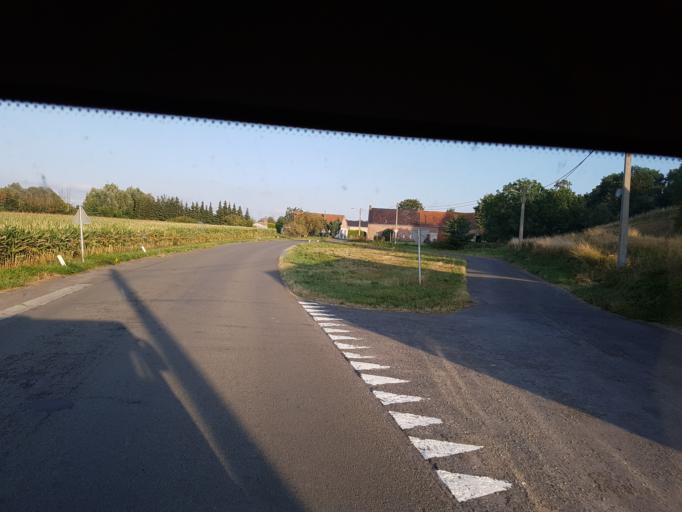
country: FR
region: Nord-Pas-de-Calais
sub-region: Departement du Nord
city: Flines-les-Mortagne
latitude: 50.5438
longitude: 3.5017
